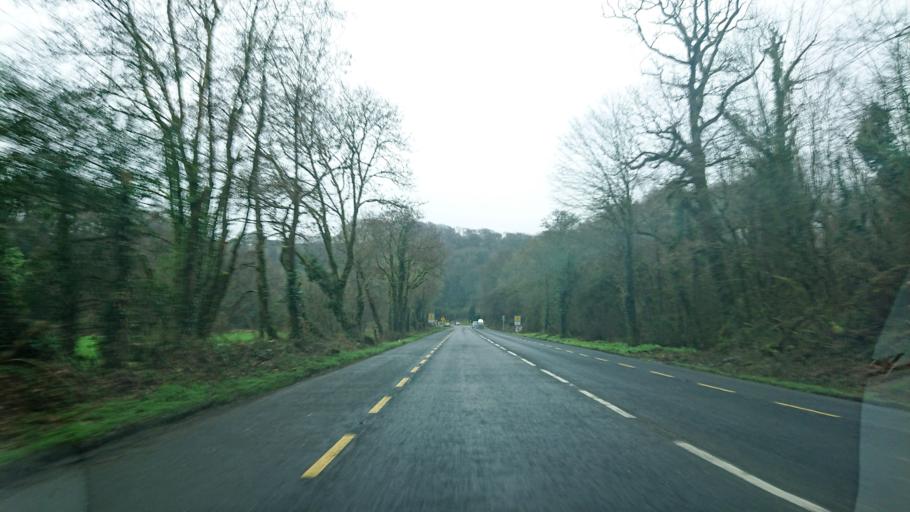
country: IE
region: Munster
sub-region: County Cork
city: Bandon
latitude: 51.7670
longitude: -8.6856
